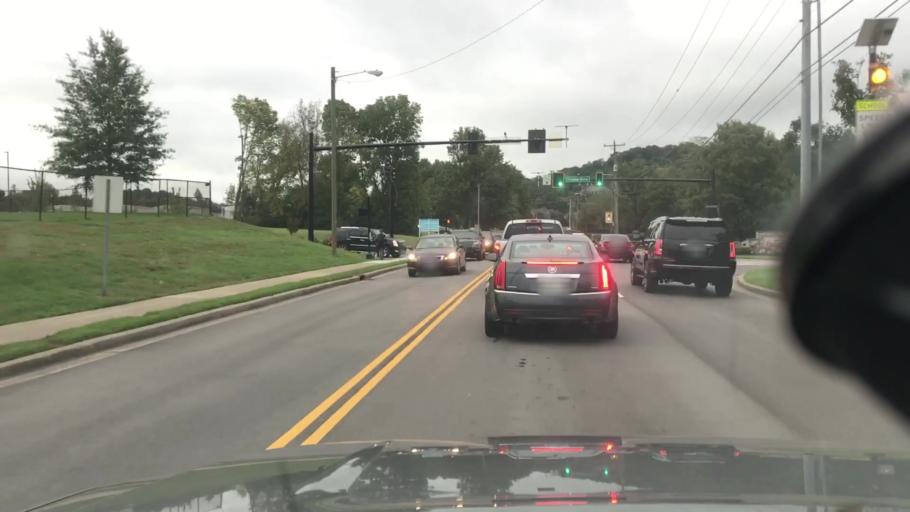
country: US
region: Tennessee
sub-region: Williamson County
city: Brentwood
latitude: 36.0195
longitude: -86.8207
